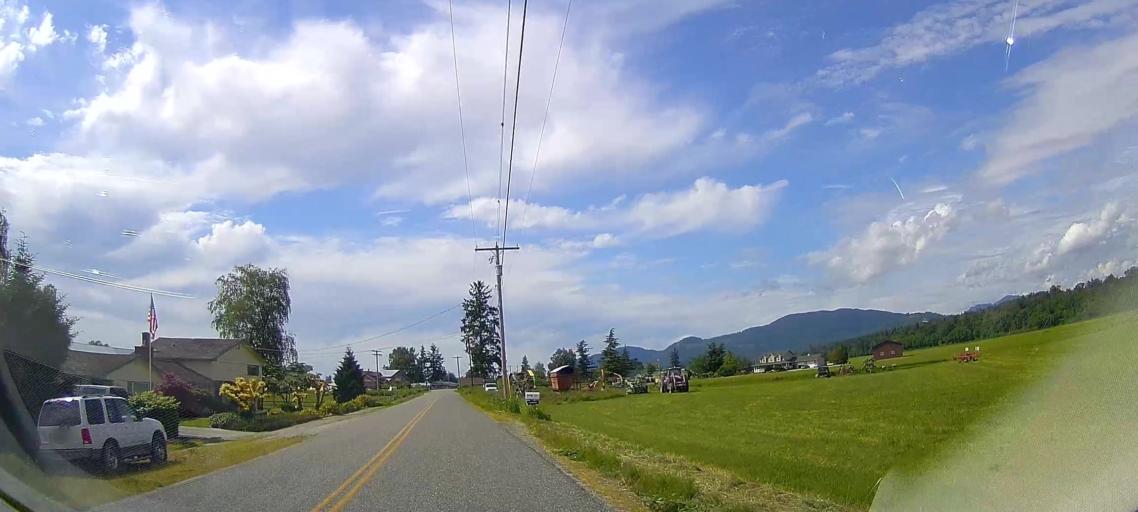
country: US
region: Washington
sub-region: Skagit County
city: Burlington
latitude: 48.5393
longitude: -122.3891
